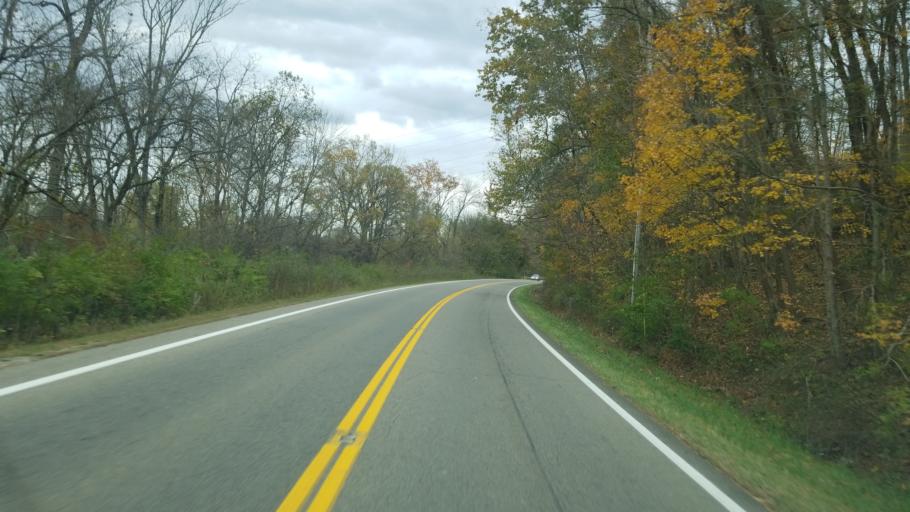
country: US
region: Ohio
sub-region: Pike County
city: Piketon
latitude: 39.0078
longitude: -83.0522
